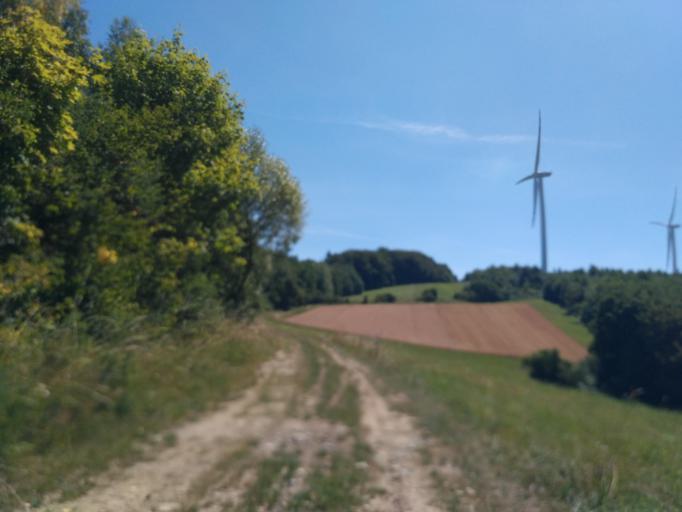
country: PL
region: Subcarpathian Voivodeship
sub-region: Powiat sanocki
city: Bukowsko
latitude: 49.5140
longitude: 22.0516
